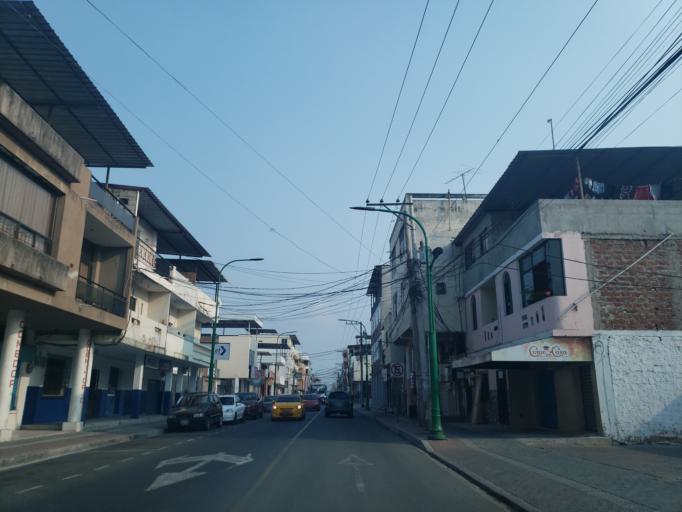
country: EC
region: Manabi
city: Manta
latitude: -0.9463
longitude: -80.7337
